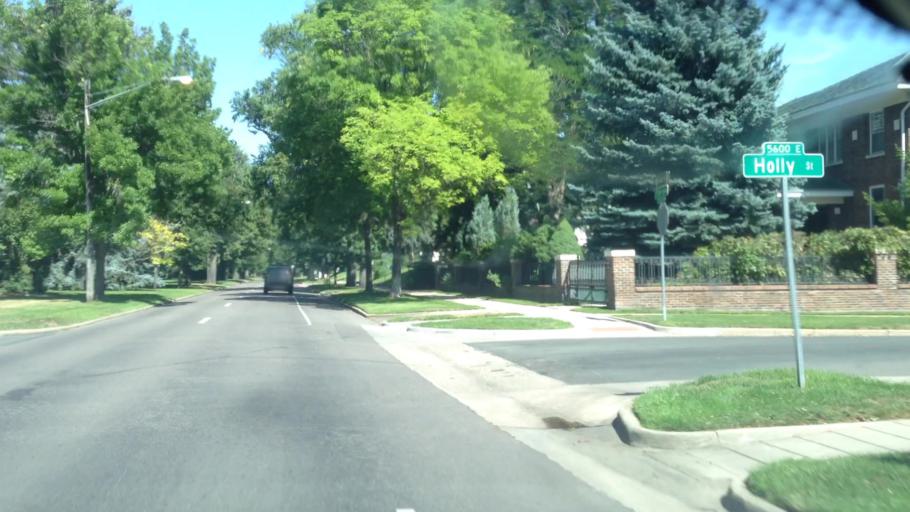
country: US
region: Colorado
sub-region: Arapahoe County
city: Glendale
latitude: 39.7434
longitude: -104.9226
